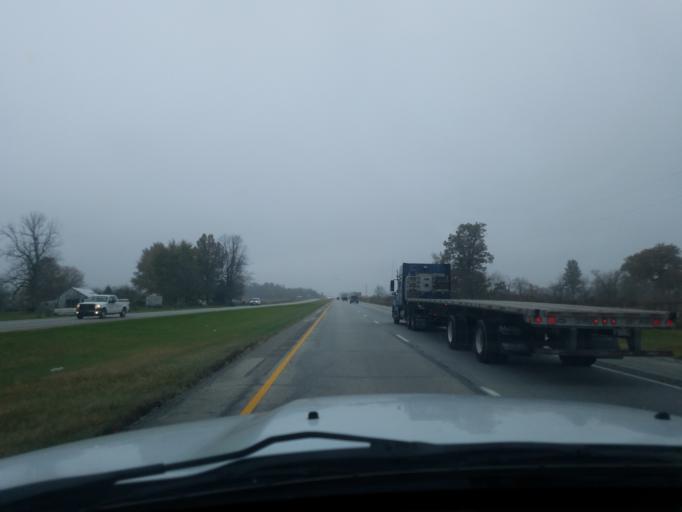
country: US
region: Indiana
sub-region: Hamilton County
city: Sheridan
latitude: 40.1527
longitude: -86.1278
